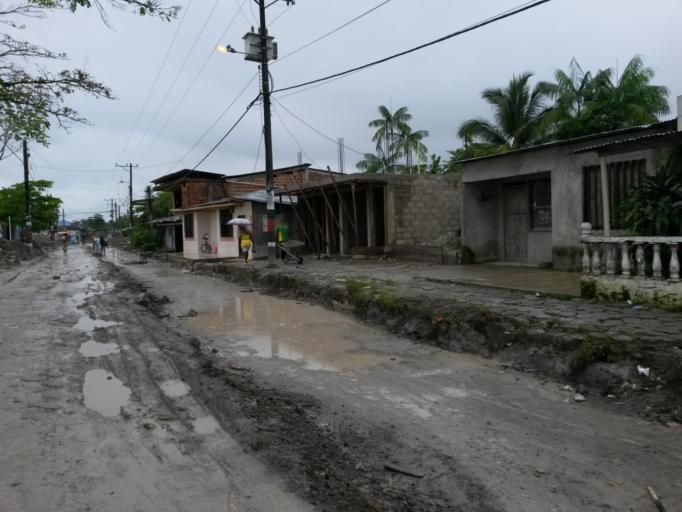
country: CO
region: Cauca
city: Guapi
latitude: 2.5724
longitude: -77.8916
